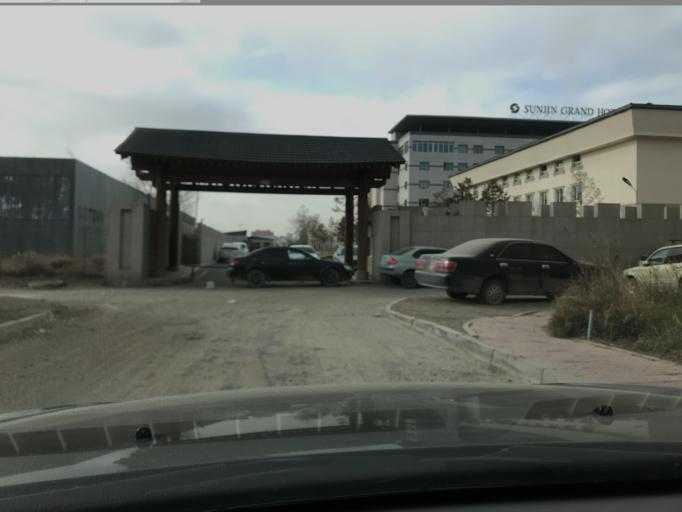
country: MN
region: Ulaanbaatar
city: Ulaanbaatar
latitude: 47.9126
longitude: 106.9745
